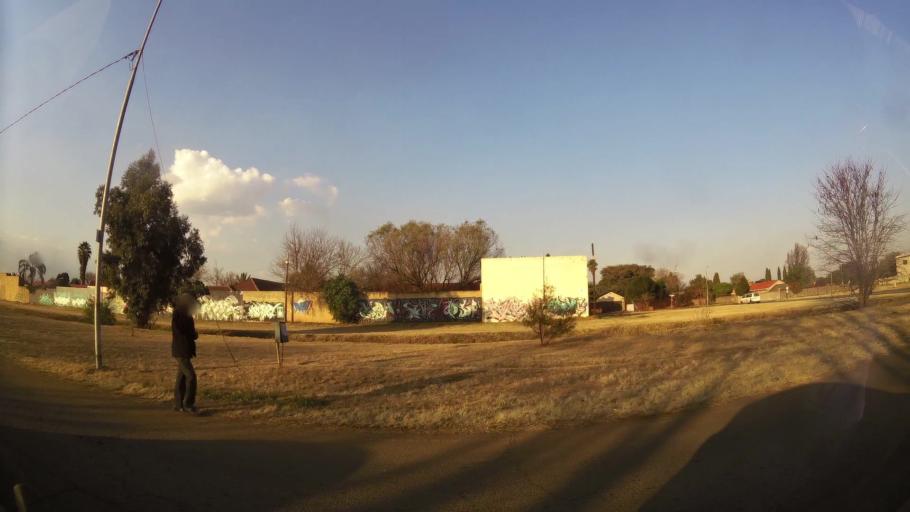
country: ZA
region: Gauteng
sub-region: Ekurhuleni Metropolitan Municipality
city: Germiston
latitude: -26.2783
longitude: 28.2263
